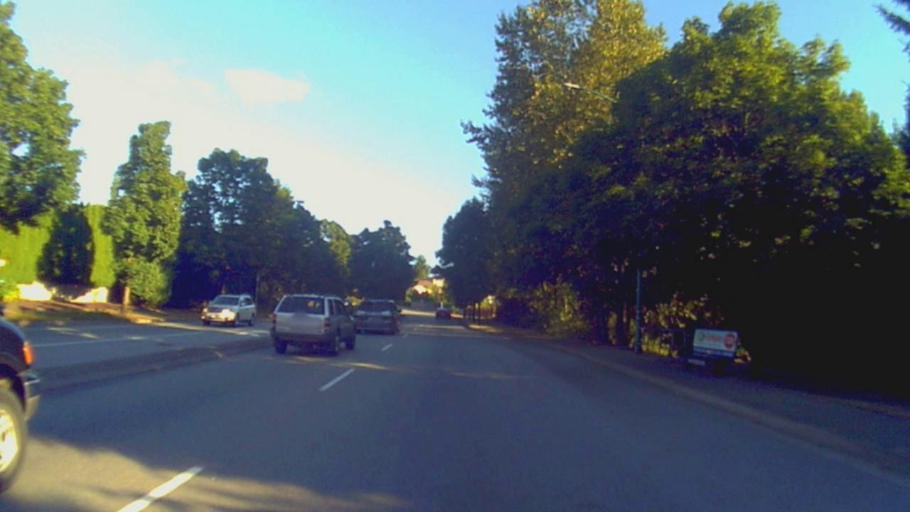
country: CA
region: British Columbia
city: New Westminster
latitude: 49.2381
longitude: -122.9069
